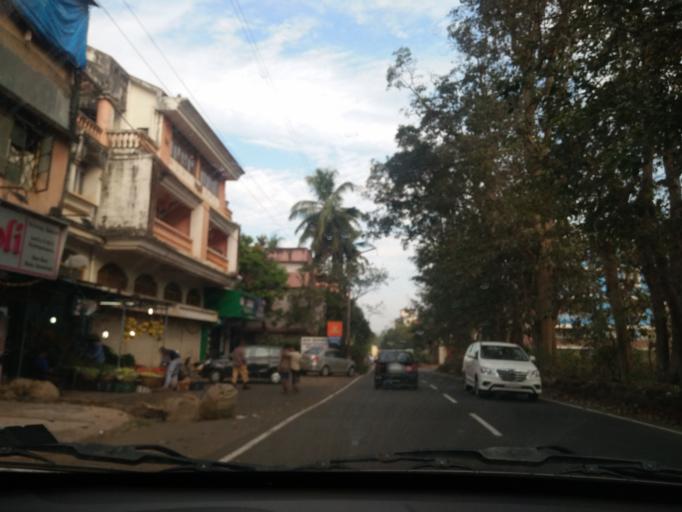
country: IN
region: Goa
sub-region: South Goa
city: Davorlim
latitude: 15.2832
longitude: 73.9782
